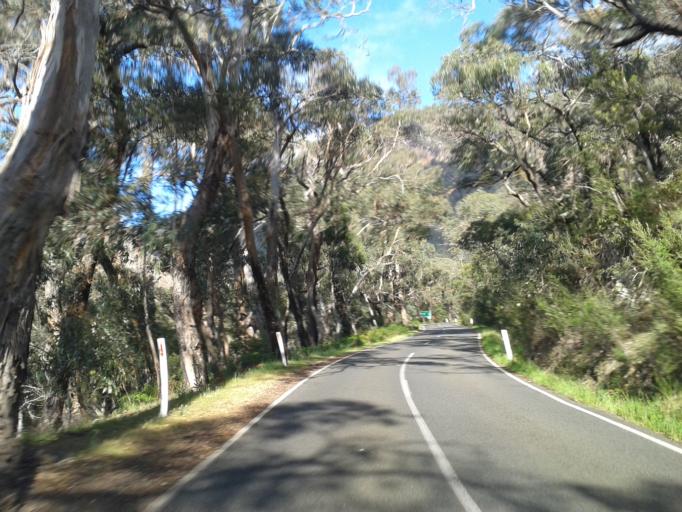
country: AU
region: Victoria
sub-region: Northern Grampians
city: Stawell
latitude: -37.1370
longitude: 142.5154
